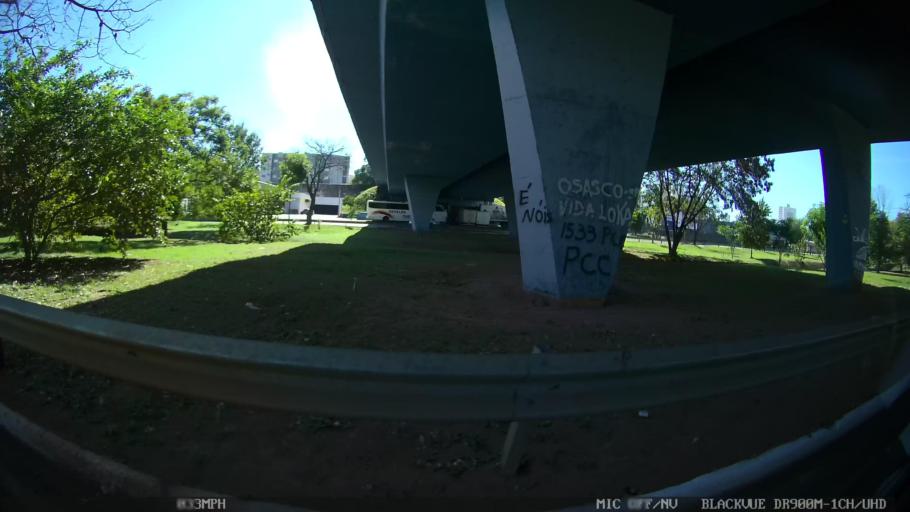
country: BR
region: Sao Paulo
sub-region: Franca
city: Franca
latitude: -20.5529
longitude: -47.4060
